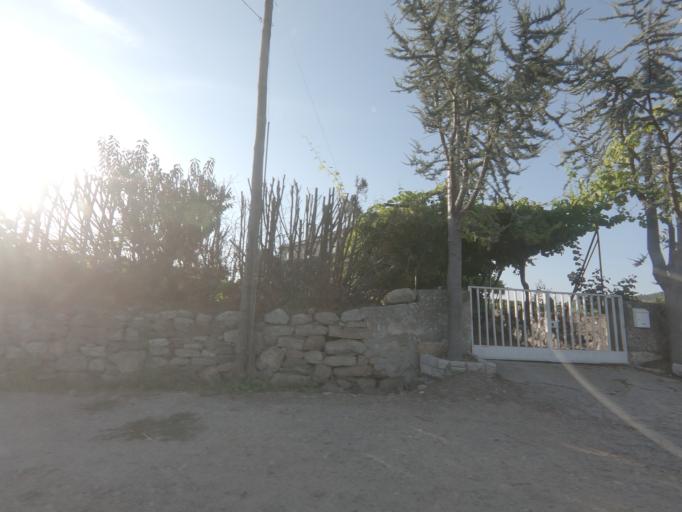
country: PT
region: Vila Real
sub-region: Sabrosa
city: Sabrosa
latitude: 41.2746
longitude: -7.5113
